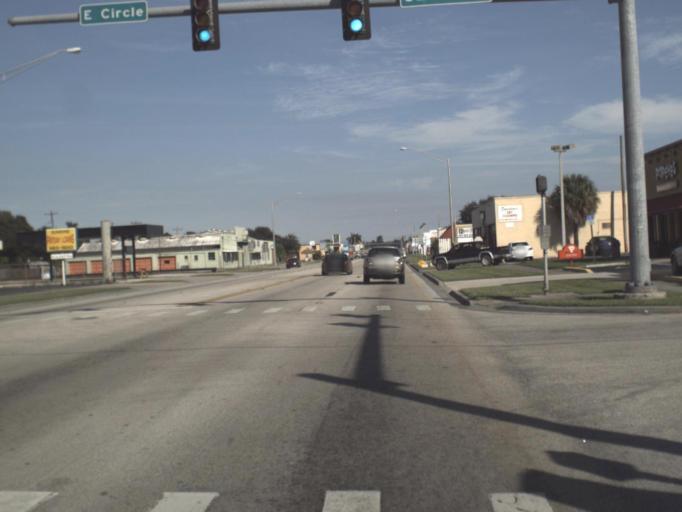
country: US
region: Florida
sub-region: Hendry County
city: Clewiston
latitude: 26.7542
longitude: -80.9283
